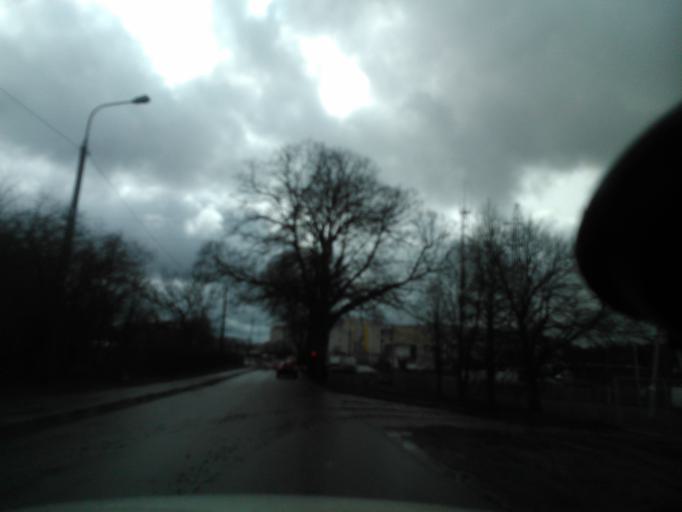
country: PL
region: Warmian-Masurian Voivodeship
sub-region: Powiat dzialdowski
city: Lidzbark
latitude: 53.2688
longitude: 19.8306
